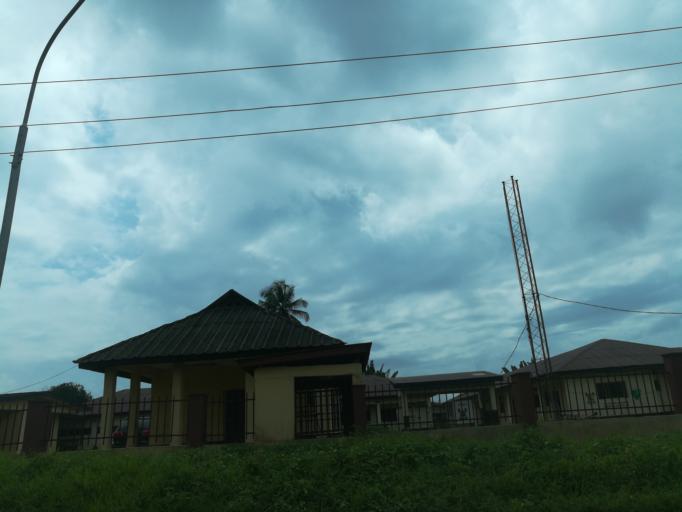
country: NG
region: Lagos
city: Ejirin
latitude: 6.6401
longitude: 3.7120
